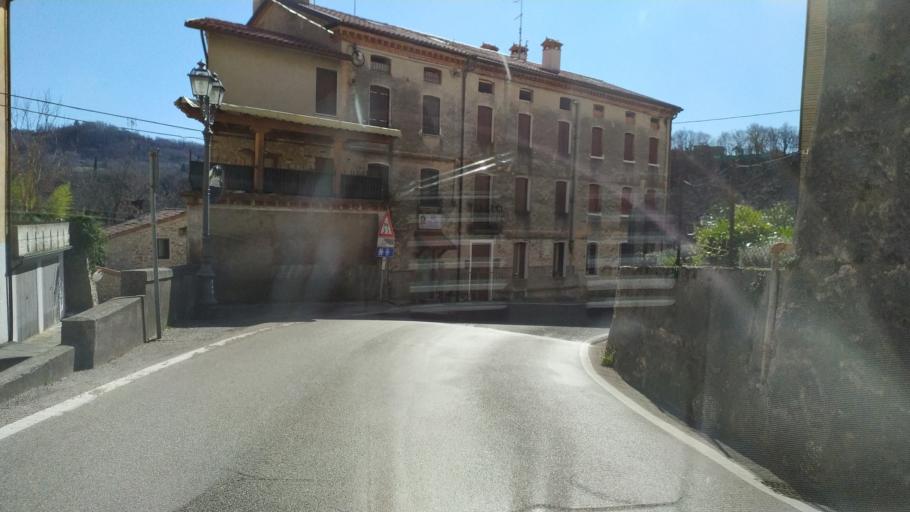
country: IT
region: Veneto
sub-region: Provincia di Vicenza
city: Caltrano
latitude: 45.7700
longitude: 11.4609
